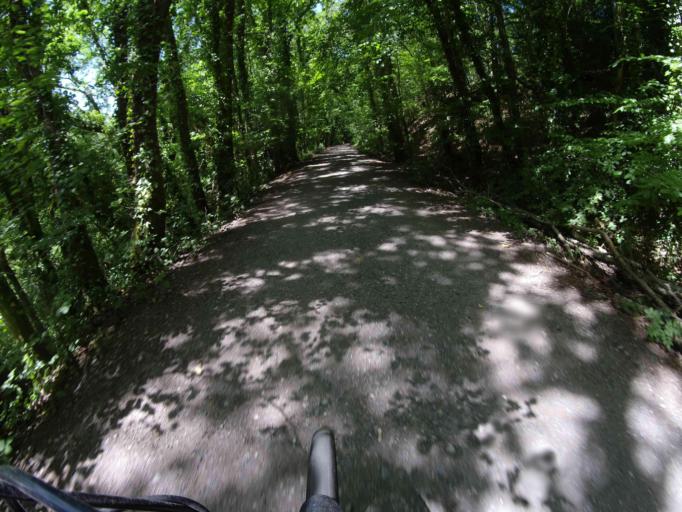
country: GB
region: England
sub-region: Devon
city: Bovey Tracey
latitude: 50.6006
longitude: -3.6945
